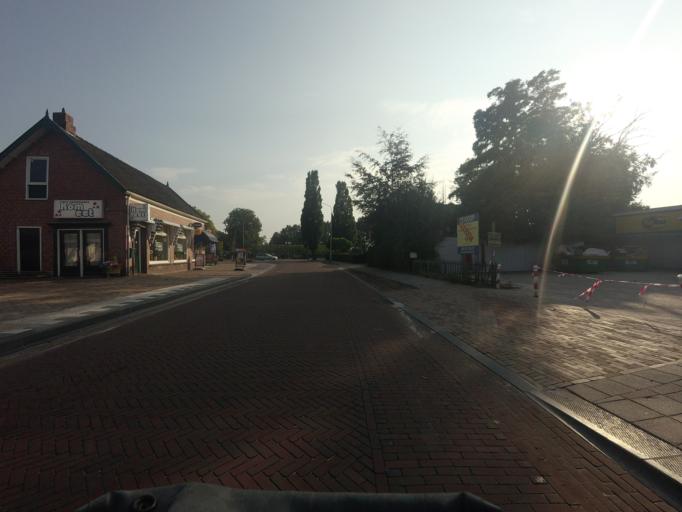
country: NL
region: Groningen
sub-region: Gemeente Haren
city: Haren
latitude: 53.1352
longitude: 6.5637
